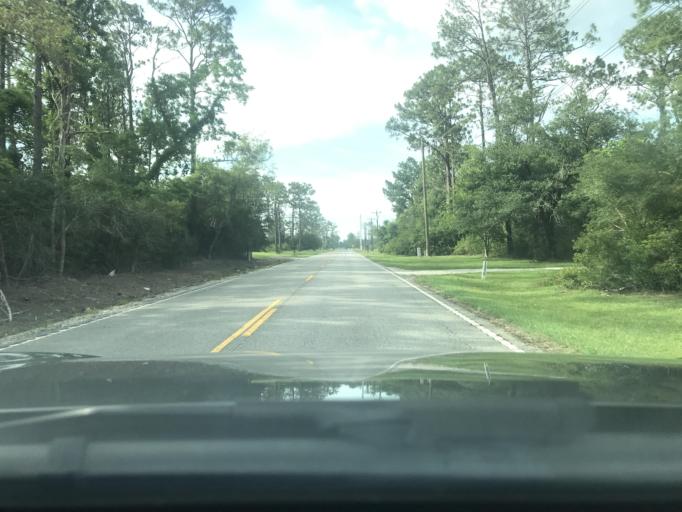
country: US
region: Louisiana
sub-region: Calcasieu Parish
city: Moss Bluff
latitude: 30.3248
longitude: -93.2582
